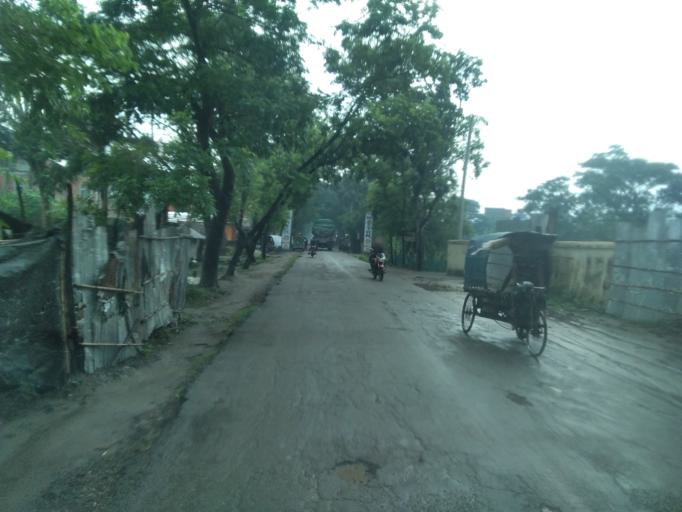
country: IN
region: West Bengal
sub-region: North 24 Parganas
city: Taki
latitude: 22.3501
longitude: 89.1031
